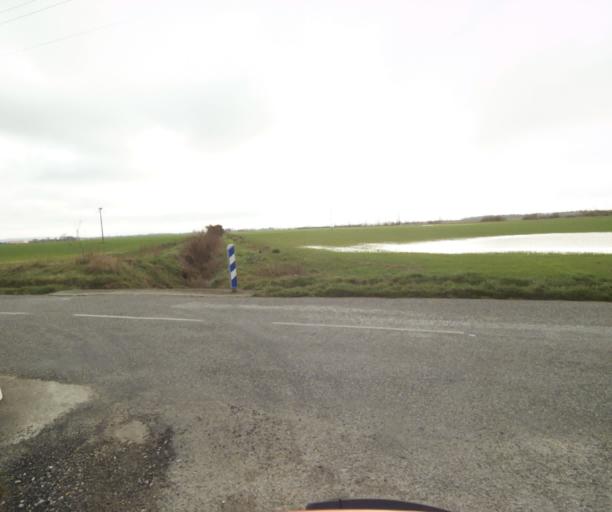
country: FR
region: Midi-Pyrenees
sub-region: Departement de l'Ariege
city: Mazeres
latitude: 43.2204
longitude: 1.7095
